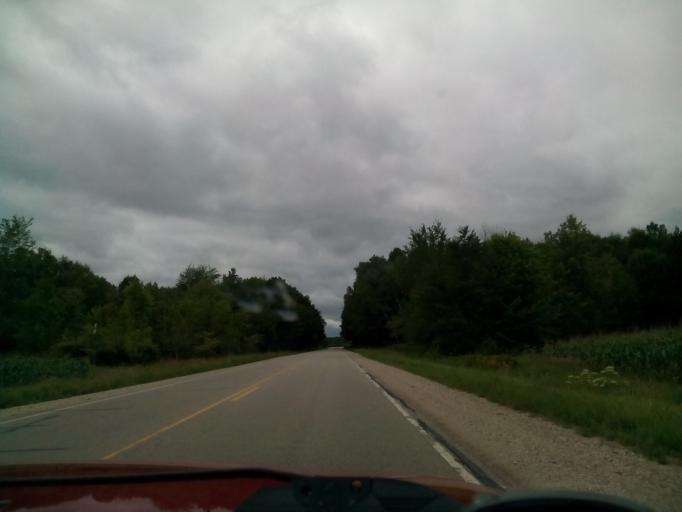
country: US
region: Wisconsin
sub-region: Menominee County
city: Legend Lake
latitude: 44.9962
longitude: -88.4382
